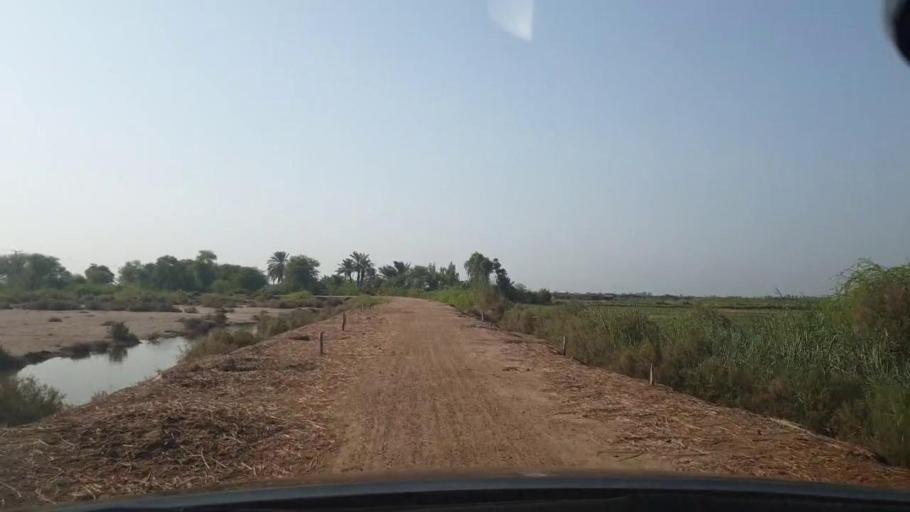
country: PK
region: Sindh
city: Tando Bago
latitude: 24.6495
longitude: 69.1477
